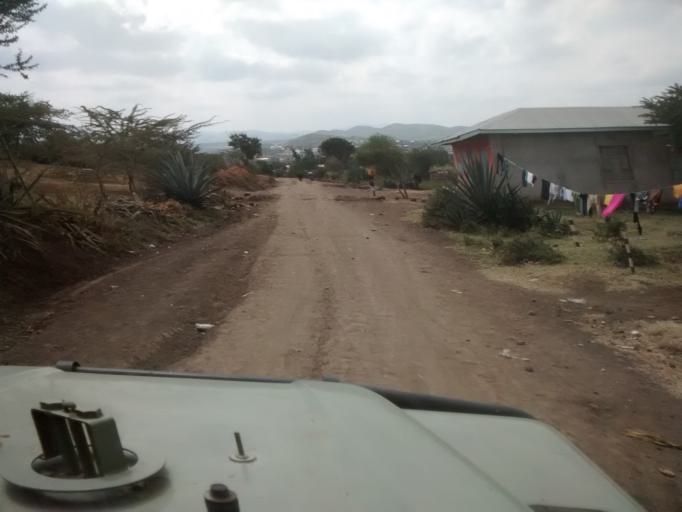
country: TZ
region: Arusha
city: Arusha
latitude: -3.3898
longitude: 36.5913
